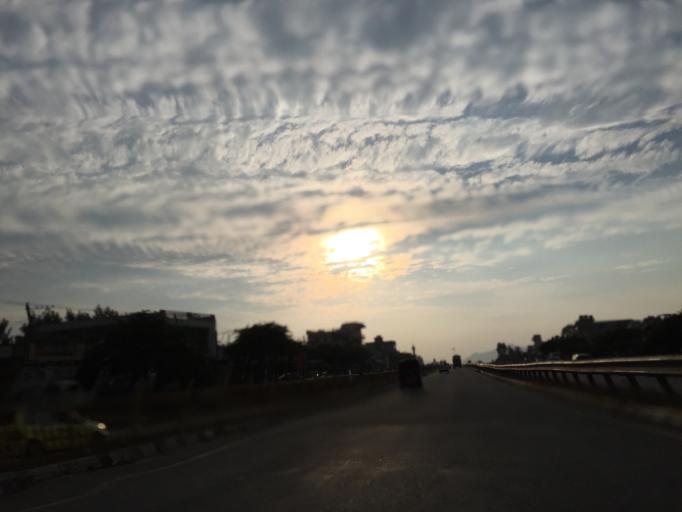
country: IN
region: Karnataka
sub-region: Kolar
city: Kolar
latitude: 13.1323
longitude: 78.1660
